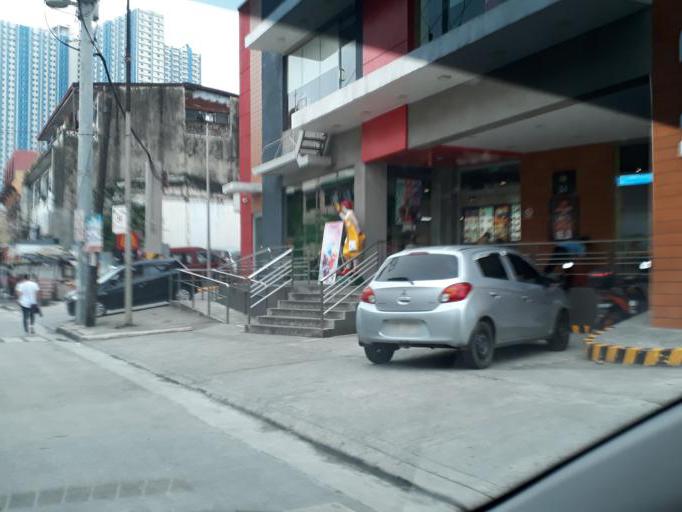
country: PH
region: Metro Manila
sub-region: City of Manila
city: Manila
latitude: 14.6220
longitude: 120.9997
